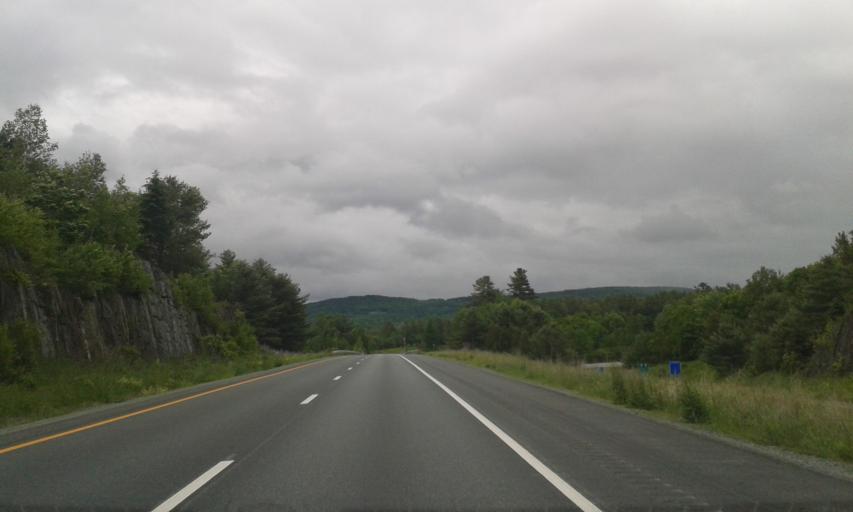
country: US
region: New Hampshire
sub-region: Grafton County
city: Littleton
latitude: 44.3305
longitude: -71.8778
